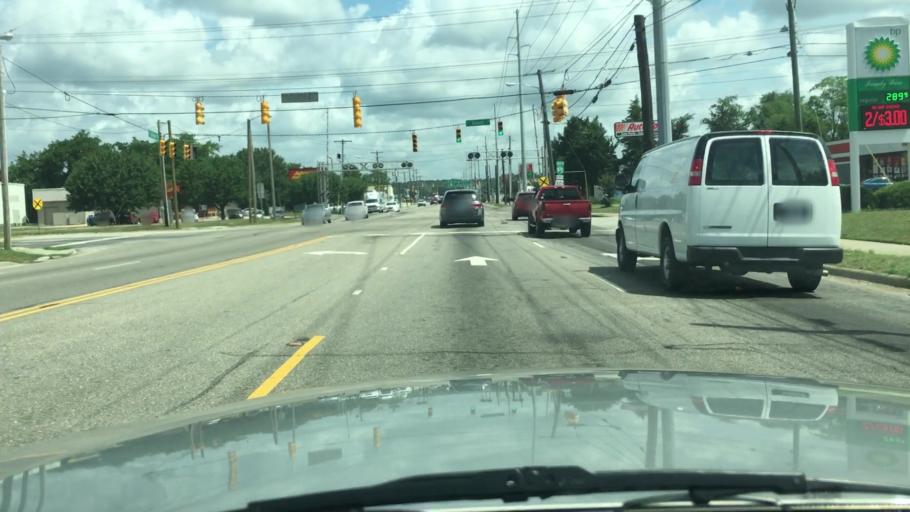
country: US
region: North Carolina
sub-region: Cumberland County
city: Fayetteville
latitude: 35.0455
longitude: -78.8656
